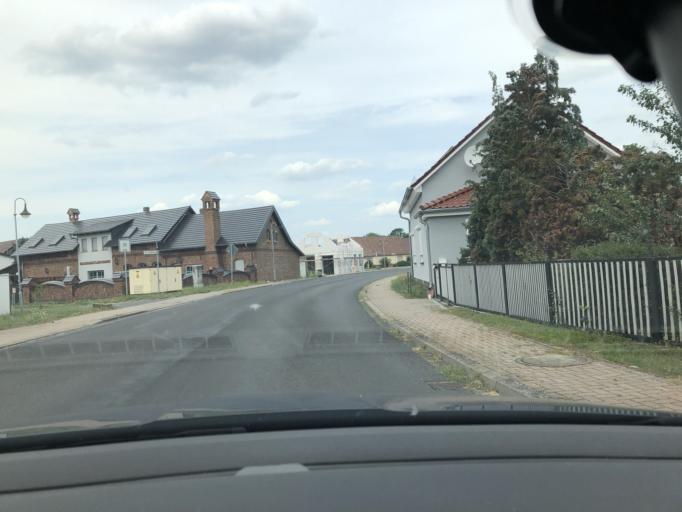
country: DE
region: Brandenburg
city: Kasel-Golzig
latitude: 51.9627
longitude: 13.7443
